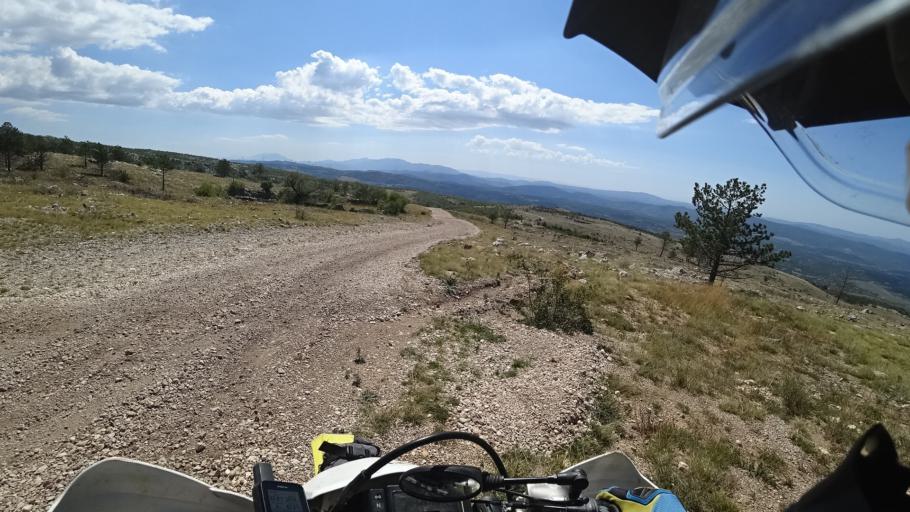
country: HR
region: Splitsko-Dalmatinska
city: Hrvace
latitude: 43.7713
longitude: 16.4654
